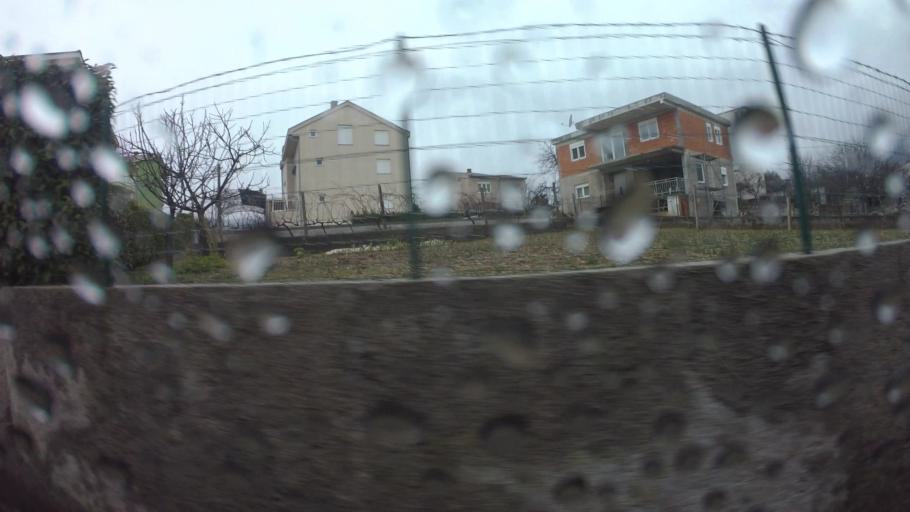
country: BA
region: Federation of Bosnia and Herzegovina
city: Cim
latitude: 43.3504
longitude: 17.7826
